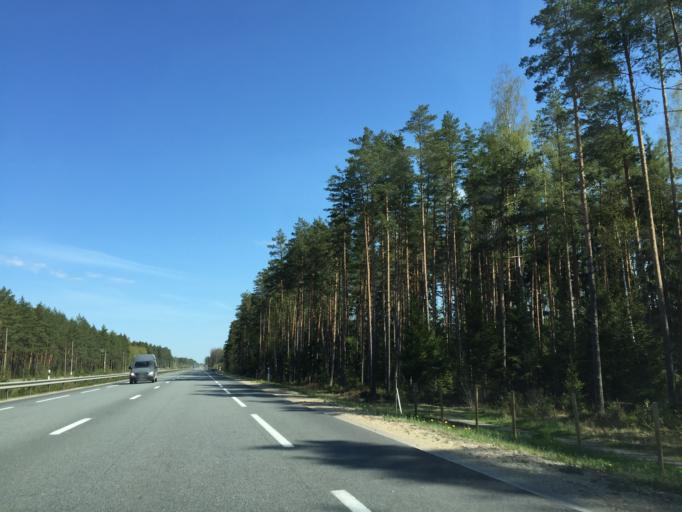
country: LV
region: Saulkrastu
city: Saulkrasti
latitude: 57.2931
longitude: 24.4368
